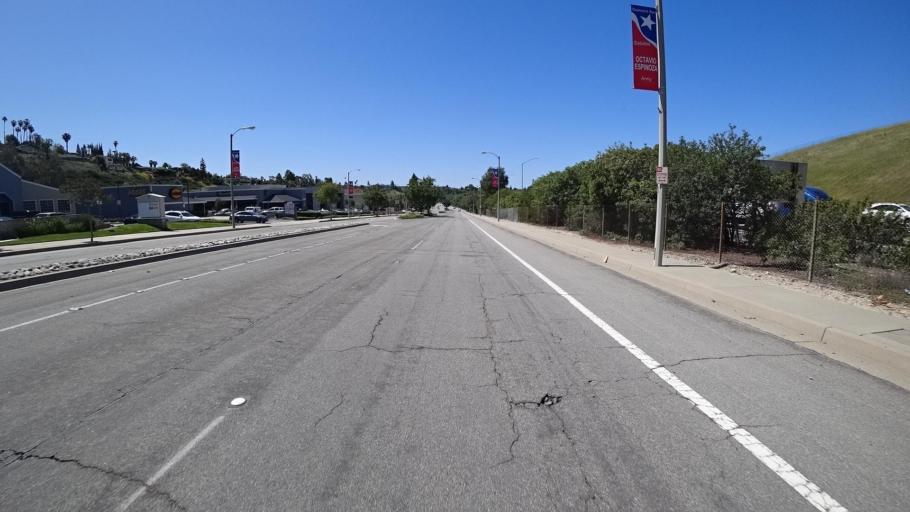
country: US
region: California
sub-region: Los Angeles County
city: Diamond Bar
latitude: 34.0340
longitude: -117.8072
